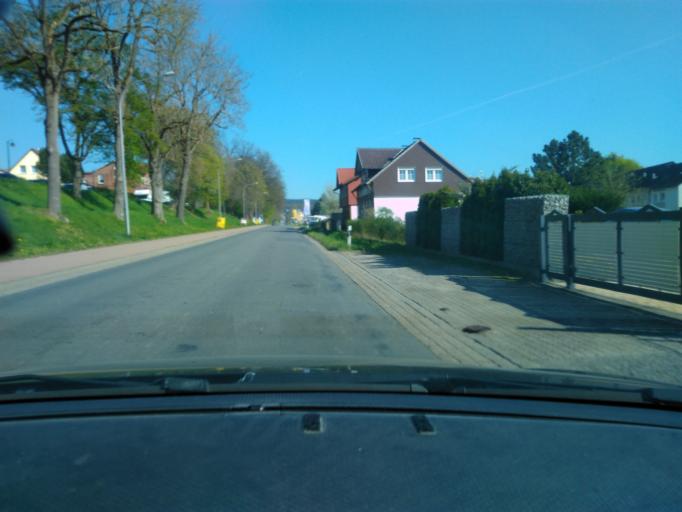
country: DE
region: Lower Saxony
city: Osterode am Harz
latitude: 51.7226
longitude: 10.2617
